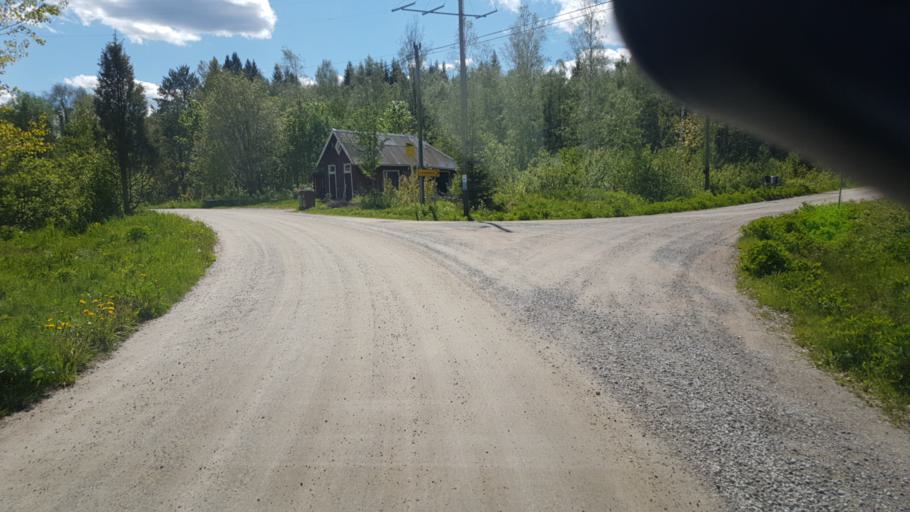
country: SE
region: Vaermland
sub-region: Sunne Kommun
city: Sunne
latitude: 59.6997
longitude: 12.8846
